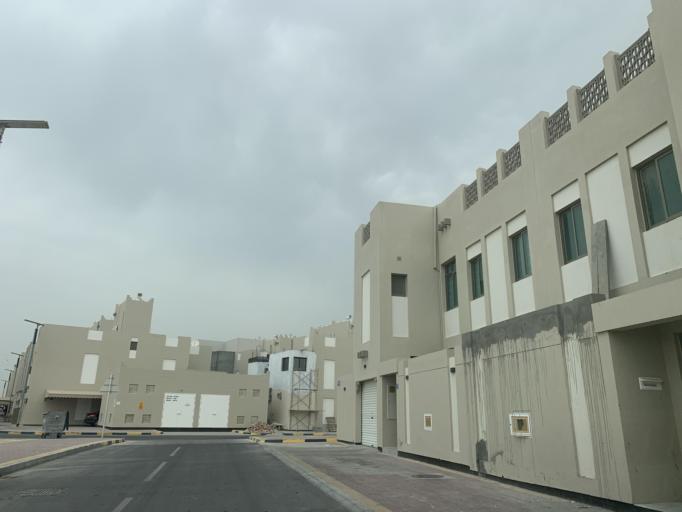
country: BH
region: Northern
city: Madinat `Isa
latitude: 26.1702
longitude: 50.5090
